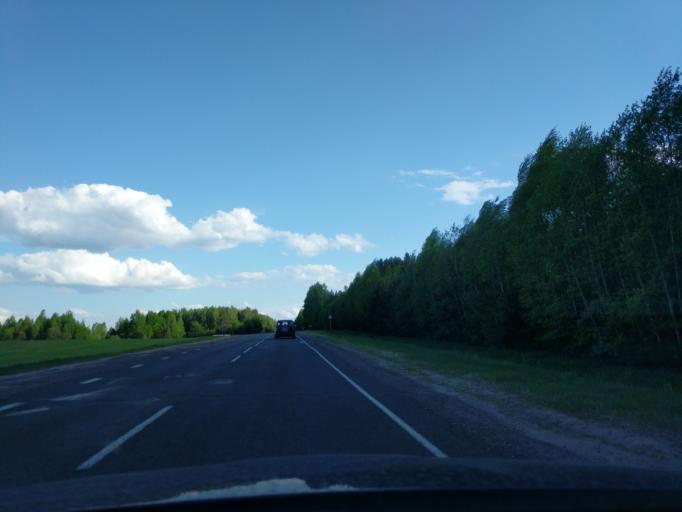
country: BY
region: Minsk
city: Kryvichy
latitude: 54.6076
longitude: 27.1809
